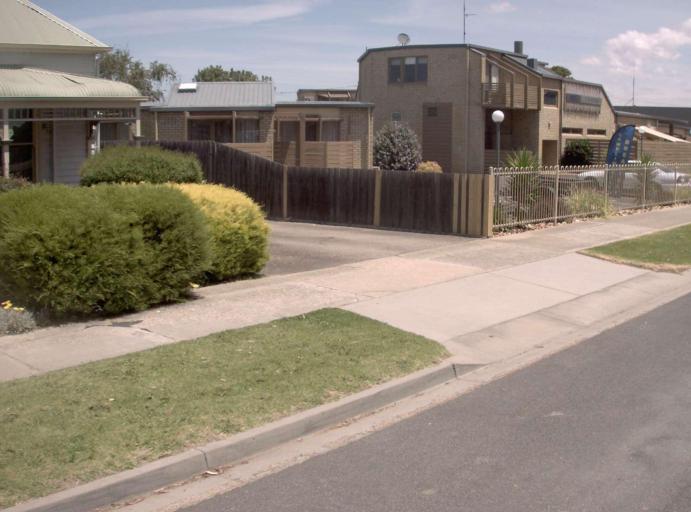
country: AU
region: Victoria
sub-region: East Gippsland
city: Bairnsdale
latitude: -37.8279
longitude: 147.6233
